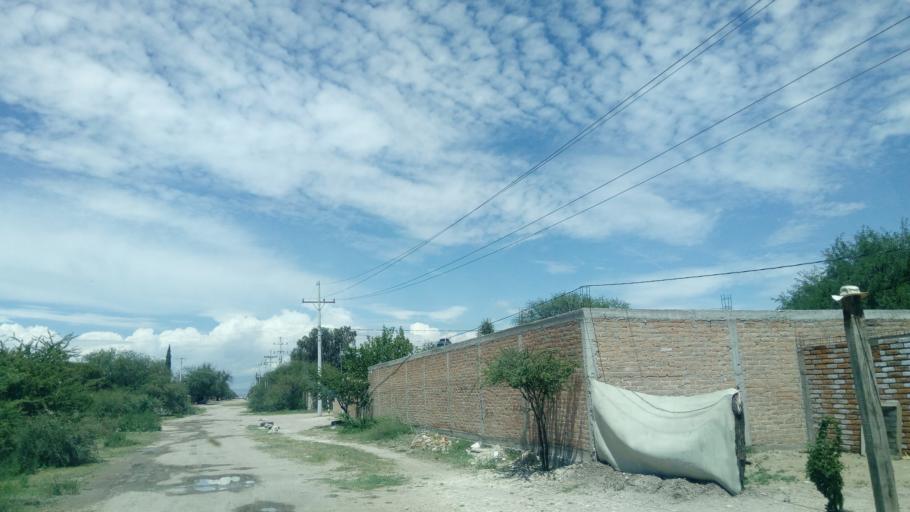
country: MX
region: Durango
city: Victoria de Durango
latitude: 24.0185
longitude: -104.5856
